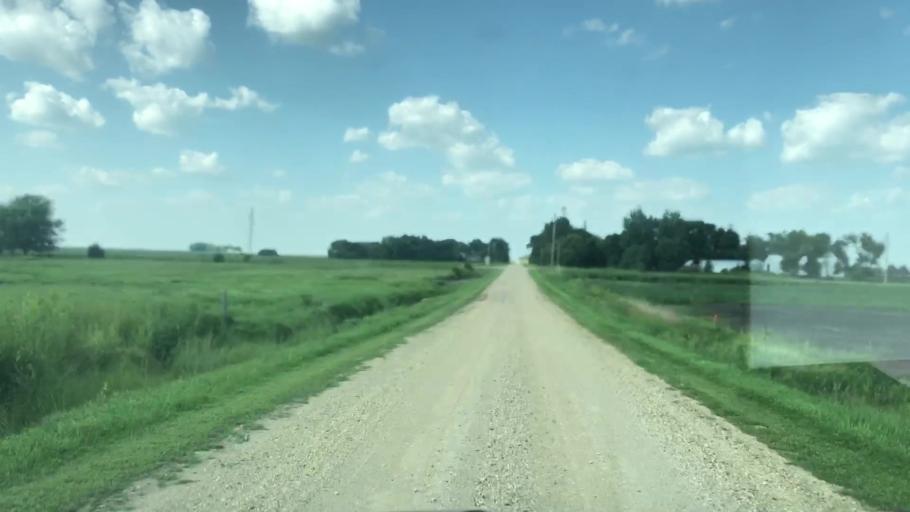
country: US
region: Iowa
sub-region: O'Brien County
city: Sheldon
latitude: 43.1697
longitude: -95.7823
